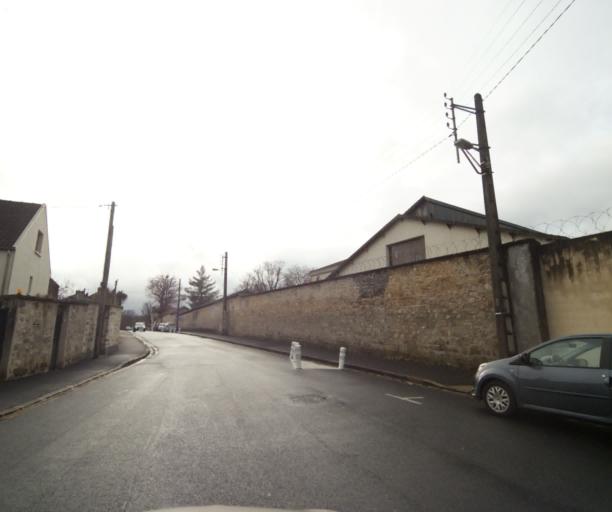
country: FR
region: Ile-de-France
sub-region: Departement de Seine-et-Marne
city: Avon
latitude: 48.4043
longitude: 2.7178
